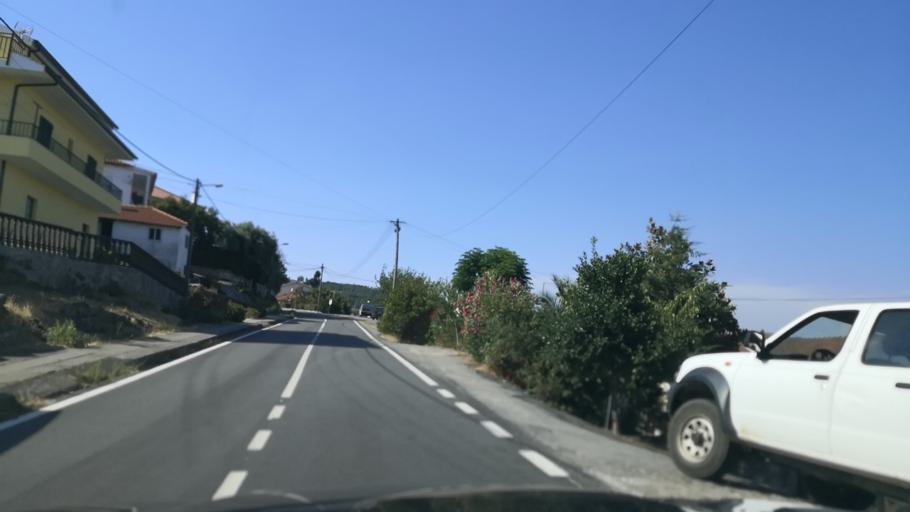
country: PT
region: Vila Real
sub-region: Sabrosa
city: Sabrosa
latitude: 41.2863
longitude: -7.4771
